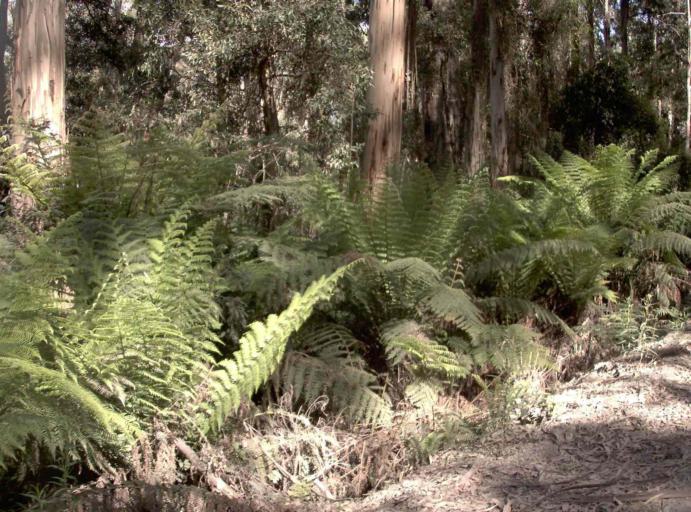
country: AU
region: New South Wales
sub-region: Bombala
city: Bombala
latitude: -37.2475
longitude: 148.7530
